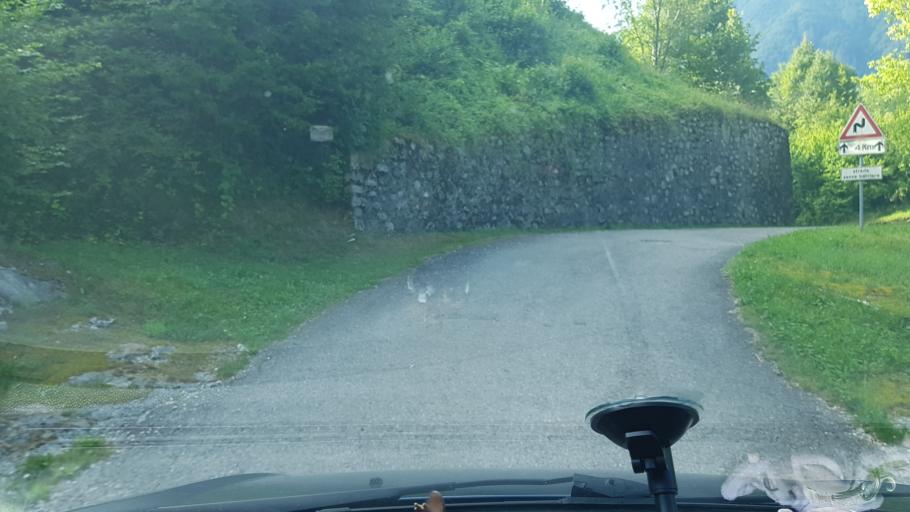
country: IT
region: Friuli Venezia Giulia
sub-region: Provincia di Udine
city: Prato
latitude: 46.3602
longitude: 13.3551
